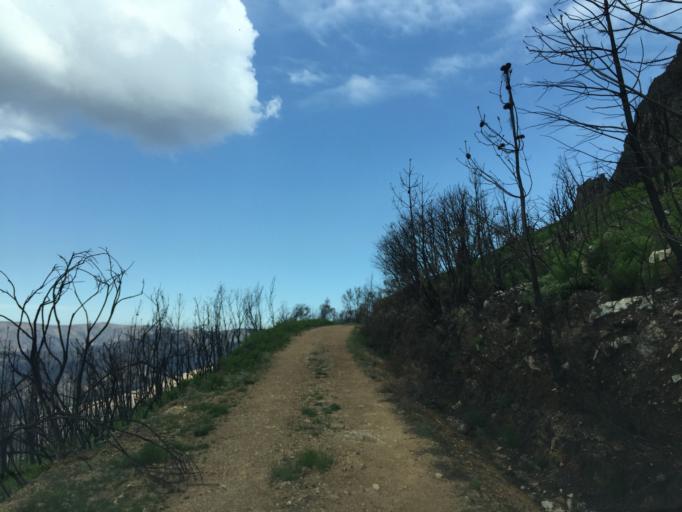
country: PT
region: Coimbra
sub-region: Pampilhosa da Serra
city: Pampilhosa da Serra
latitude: 40.1550
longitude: -7.9301
